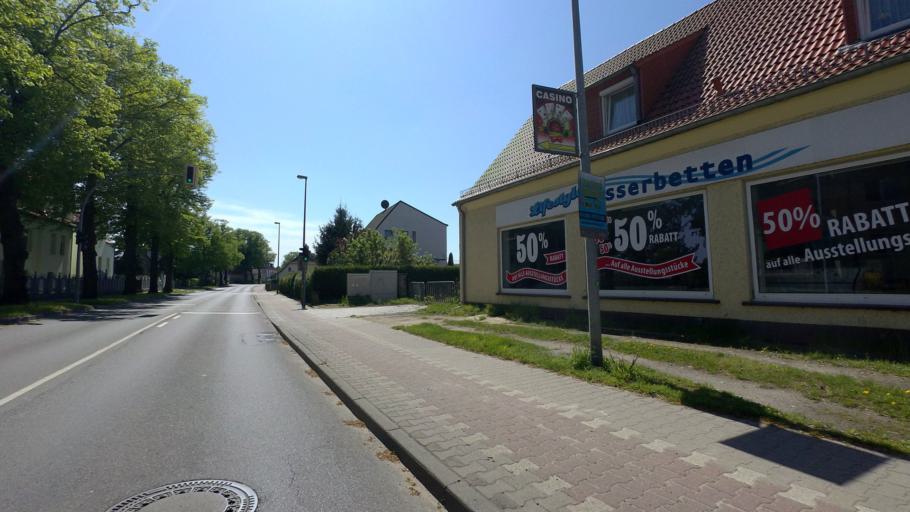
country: DE
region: Brandenburg
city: Schulzendorf
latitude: 52.3612
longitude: 13.5565
